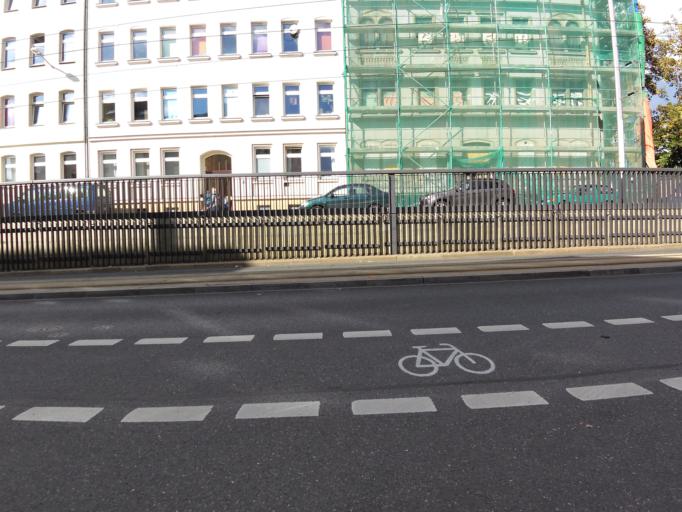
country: DE
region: Saxony
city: Leipzig
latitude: 51.3331
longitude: 12.3233
